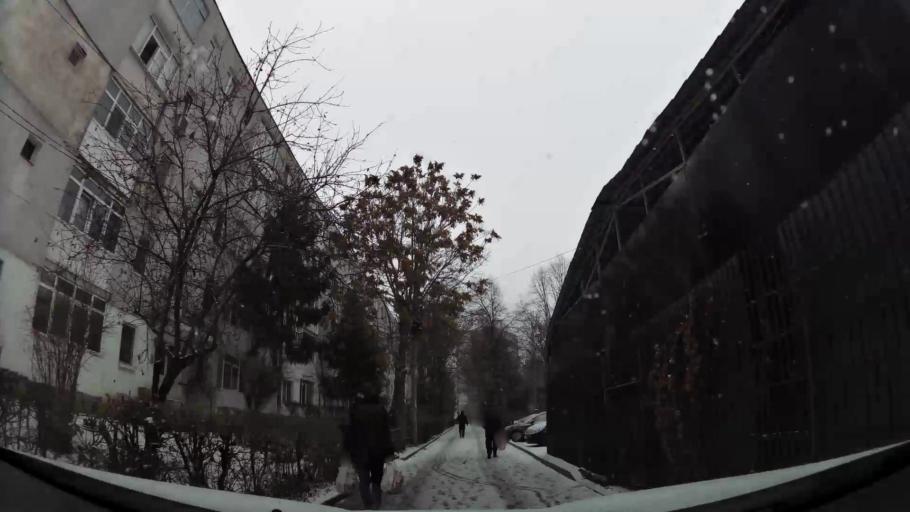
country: RO
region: Prahova
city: Ploiesti
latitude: 44.9304
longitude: 25.9958
